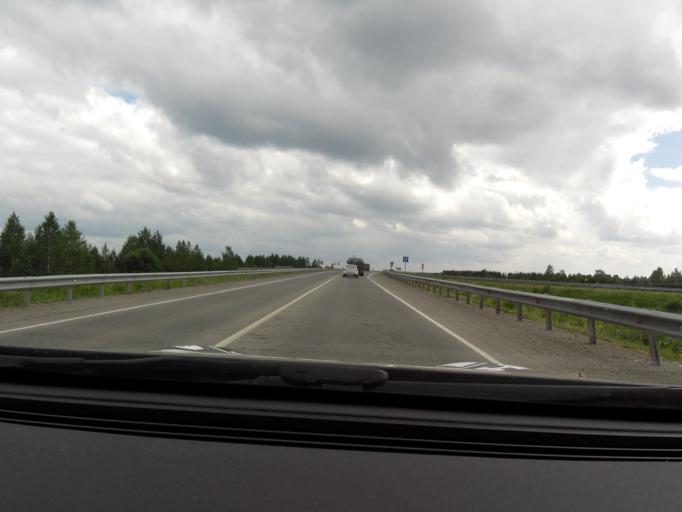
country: RU
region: Perm
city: Kungur
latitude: 57.4051
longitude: 56.8861
